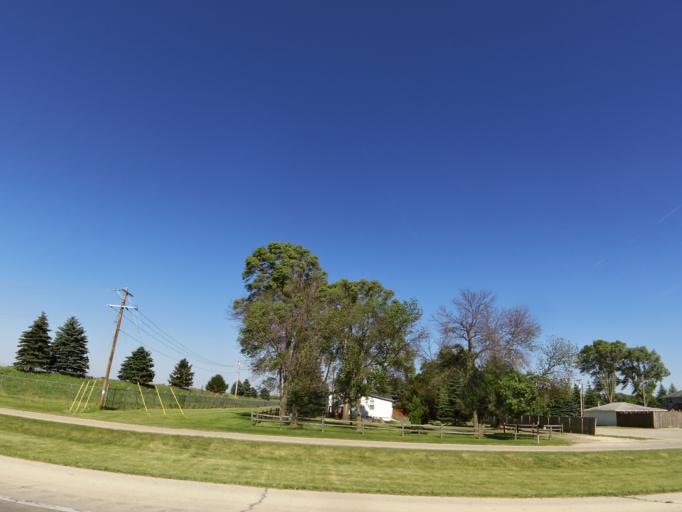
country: US
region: Illinois
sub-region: Winnebago County
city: South Beloit
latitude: 42.4720
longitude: -89.0194
